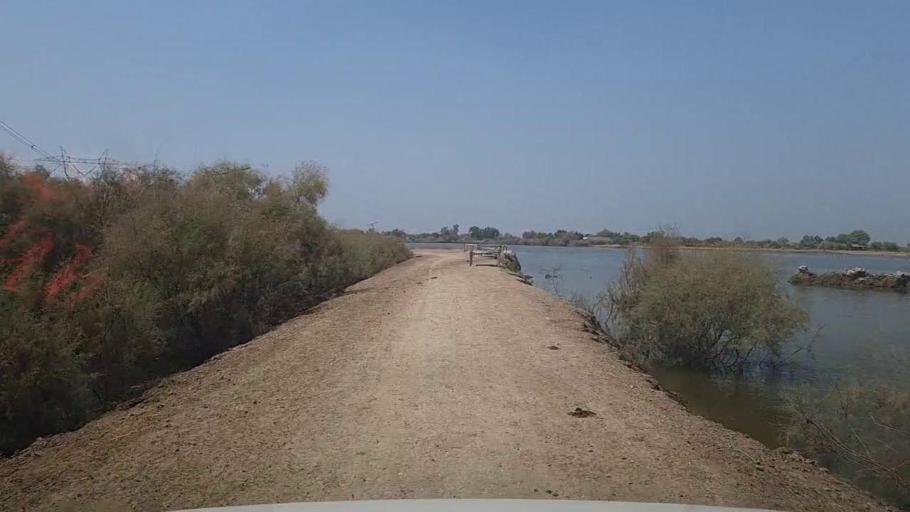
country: PK
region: Sindh
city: Kandhkot
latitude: 28.3197
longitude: 69.3738
